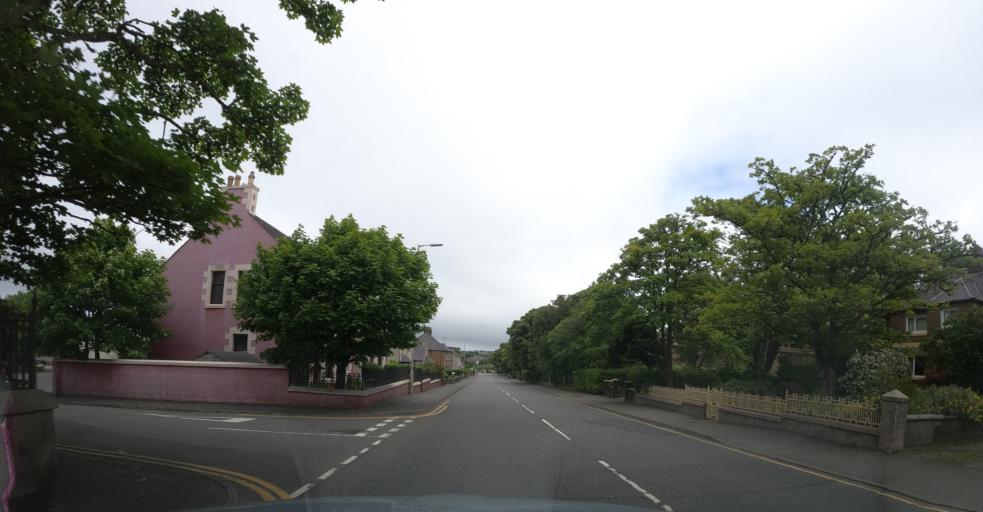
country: GB
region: Scotland
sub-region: Eilean Siar
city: Stornoway
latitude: 58.2133
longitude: -6.3837
